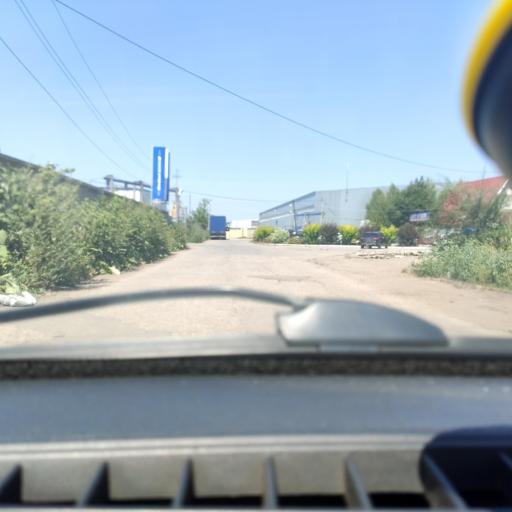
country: RU
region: Samara
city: Tol'yatti
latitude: 53.5708
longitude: 49.3610
